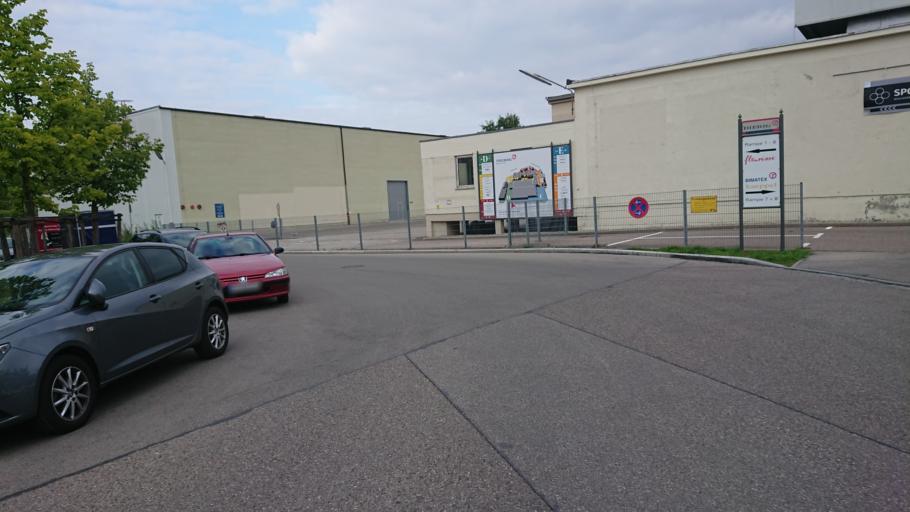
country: DE
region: Bavaria
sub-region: Swabia
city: Stadtbergen
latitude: 48.3678
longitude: 10.8697
